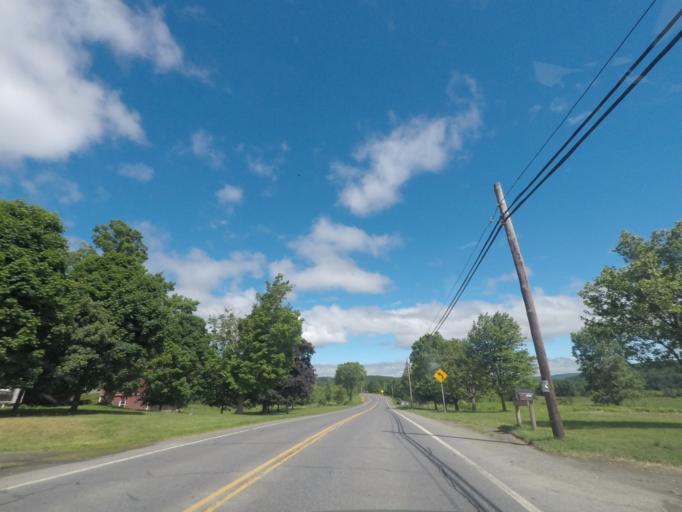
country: US
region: New York
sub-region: Columbia County
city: Philmont
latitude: 42.1749
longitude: -73.5928
